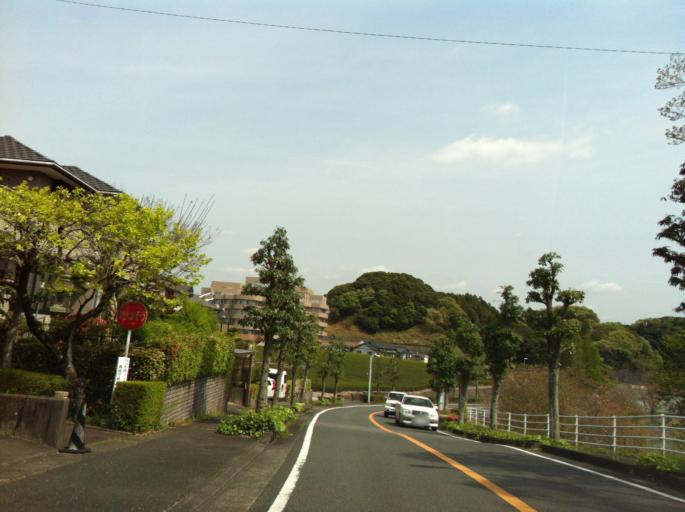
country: JP
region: Shizuoka
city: Kakegawa
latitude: 34.7846
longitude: 137.9963
